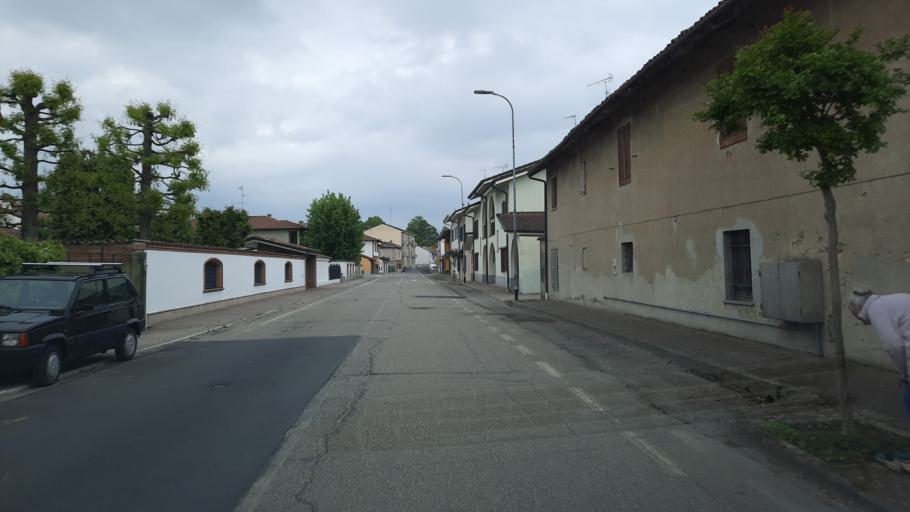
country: IT
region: Lombardy
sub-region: Provincia di Pavia
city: Robbio
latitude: 45.2896
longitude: 8.5873
